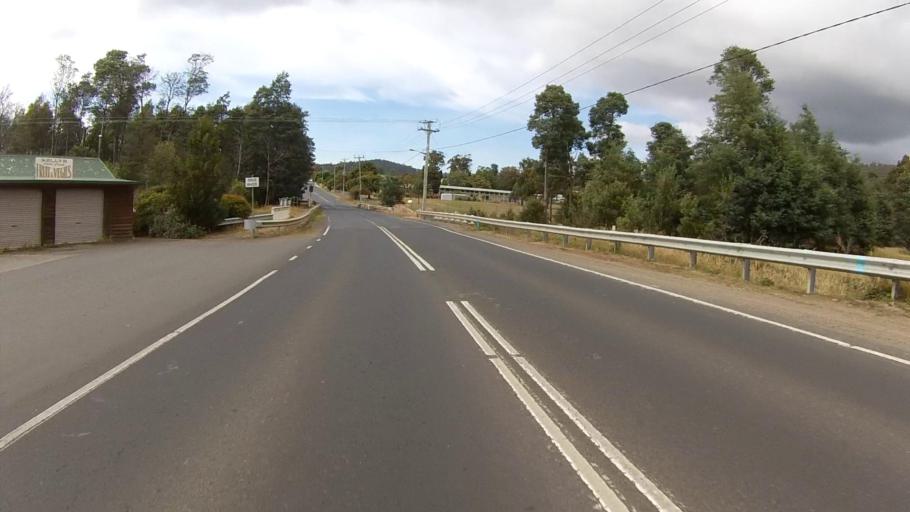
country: AU
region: Tasmania
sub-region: Kingborough
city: Margate
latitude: -43.0632
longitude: 147.2536
